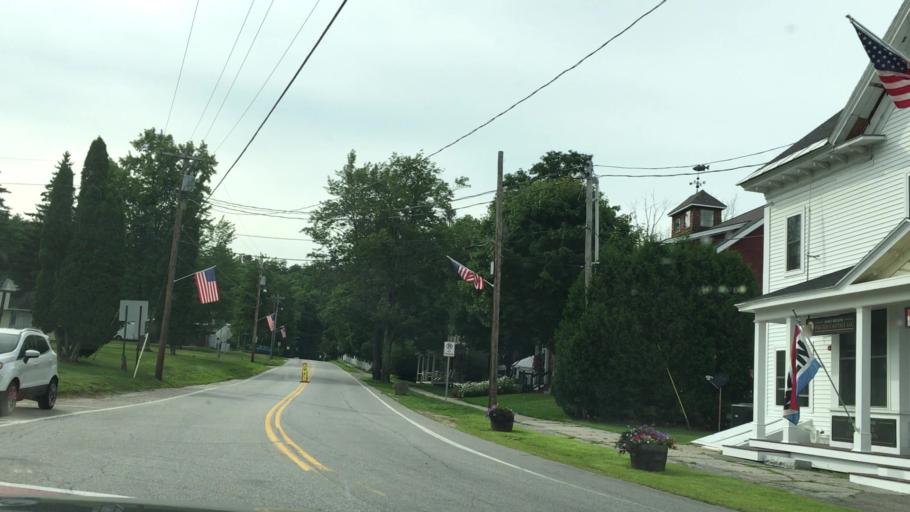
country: US
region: New Hampshire
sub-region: Carroll County
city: Center Harbor
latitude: 43.7090
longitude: -71.4628
